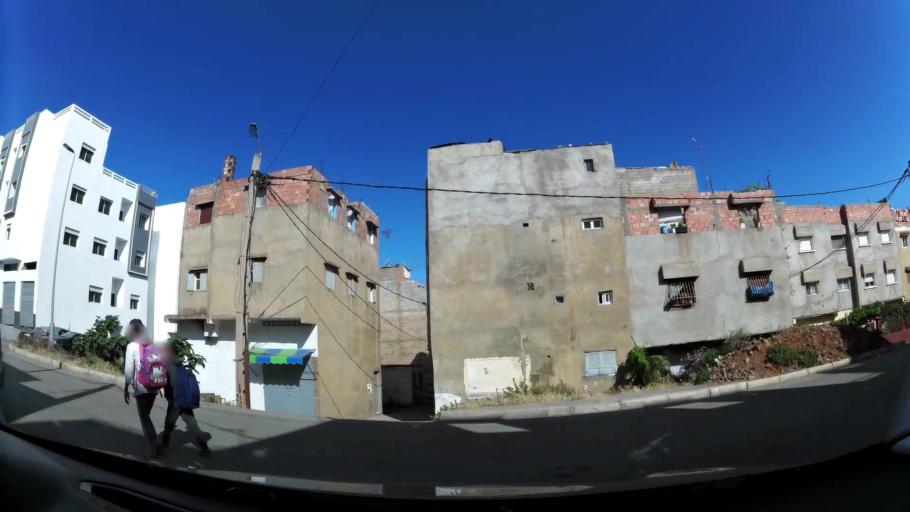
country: MA
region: Rabat-Sale-Zemmour-Zaer
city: Sale
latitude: 34.0610
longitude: -6.8100
